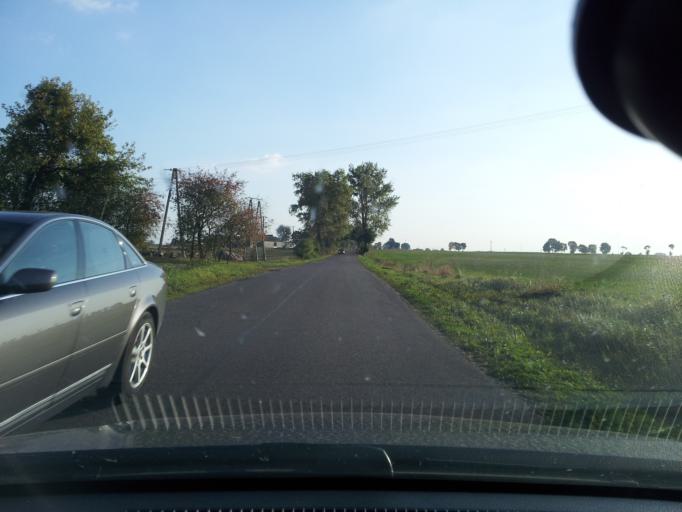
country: PL
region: Kujawsko-Pomorskie
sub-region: Powiat brodnicki
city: Bartniczka
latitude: 53.2363
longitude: 19.6006
